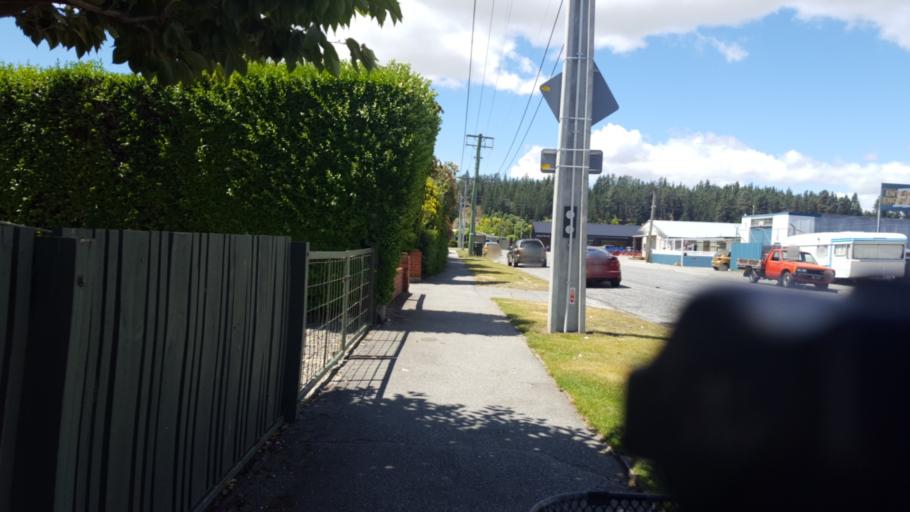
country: NZ
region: Otago
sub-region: Queenstown-Lakes District
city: Wanaka
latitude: -45.2443
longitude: 169.3906
